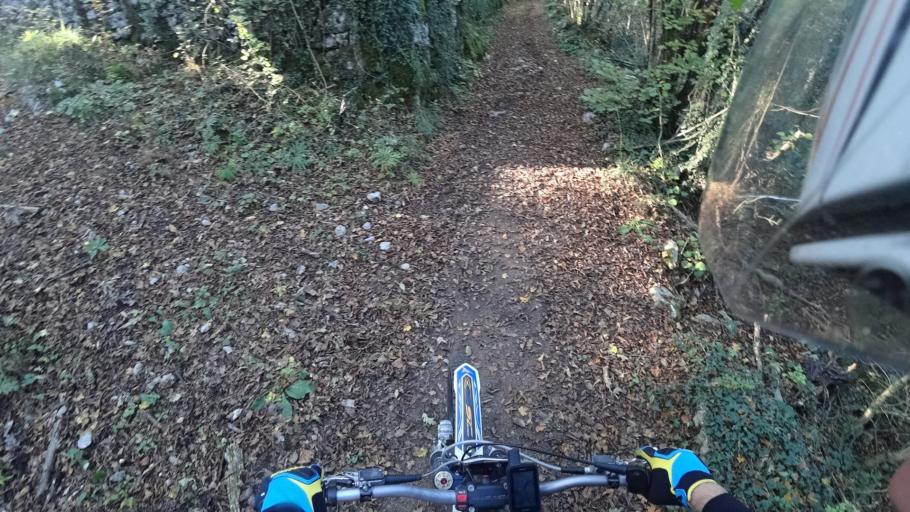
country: HR
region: Primorsko-Goranska
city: Matulji
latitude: 45.4044
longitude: 14.2876
